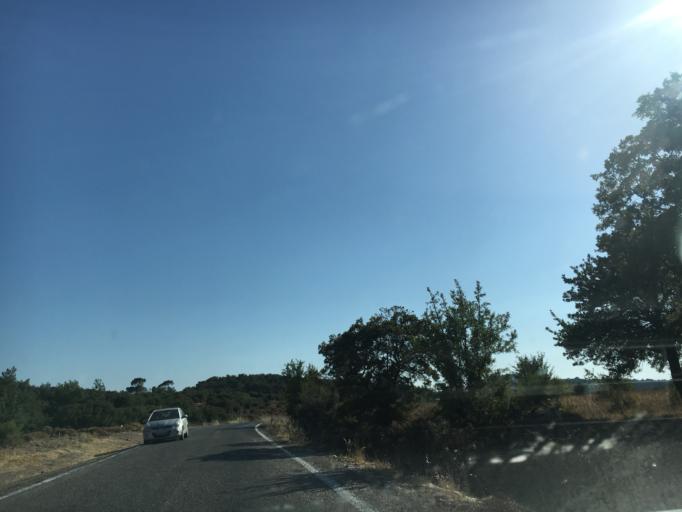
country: TR
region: Canakkale
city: Behram
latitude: 39.5006
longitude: 26.3648
